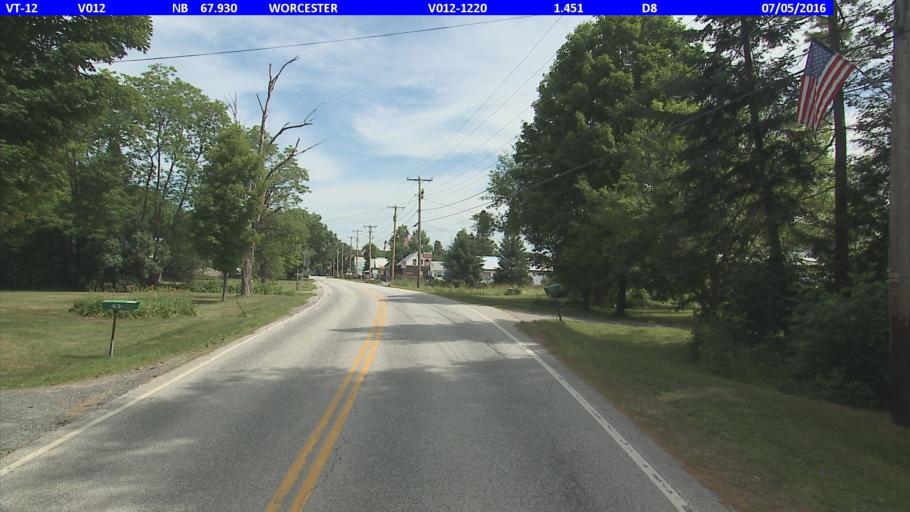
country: US
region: Vermont
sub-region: Washington County
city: Montpelier
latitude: 44.3700
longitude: -72.5510
